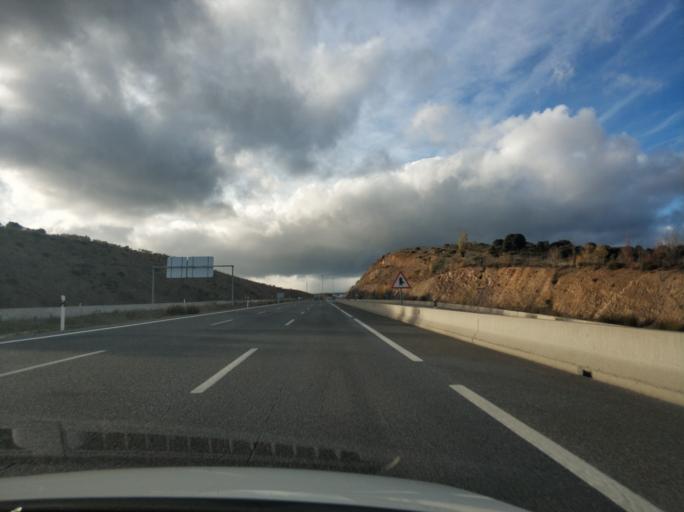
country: ES
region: Madrid
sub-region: Provincia de Madrid
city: El Vellon
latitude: 40.7503
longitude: -3.5855
